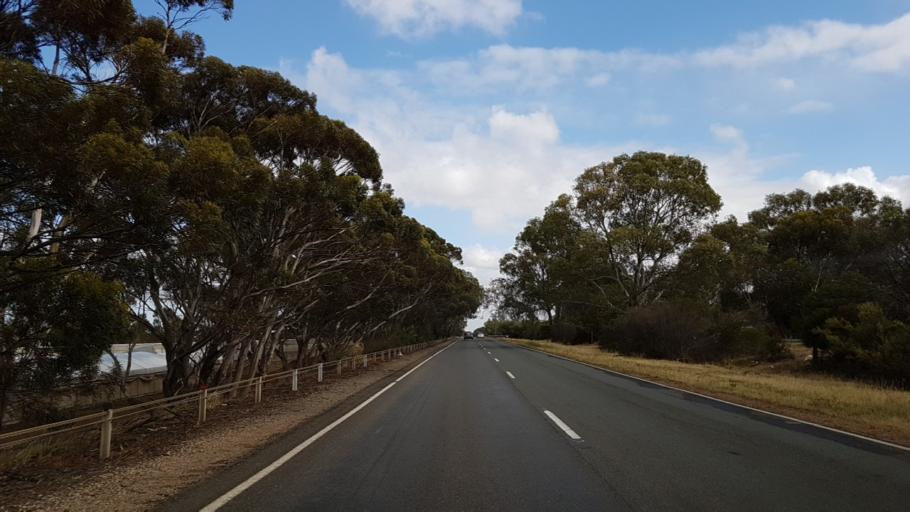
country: AU
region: South Australia
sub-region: Playford
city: Virginia
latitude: -34.6418
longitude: 138.5325
